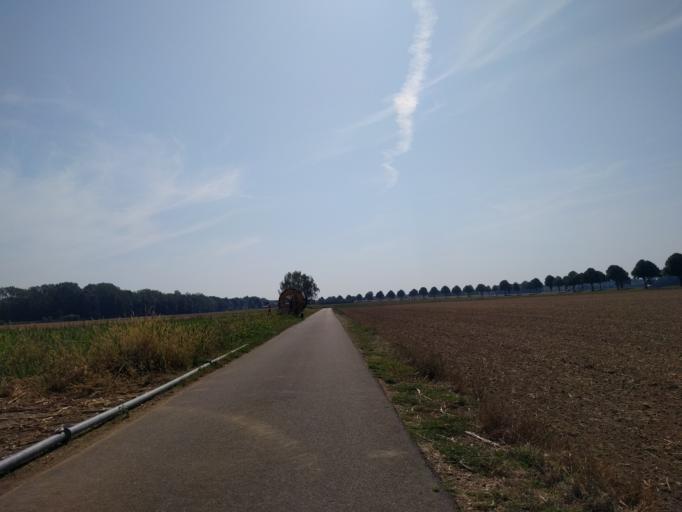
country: DE
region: Bavaria
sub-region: Upper Palatinate
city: Mintraching
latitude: 48.9855
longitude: 12.2589
